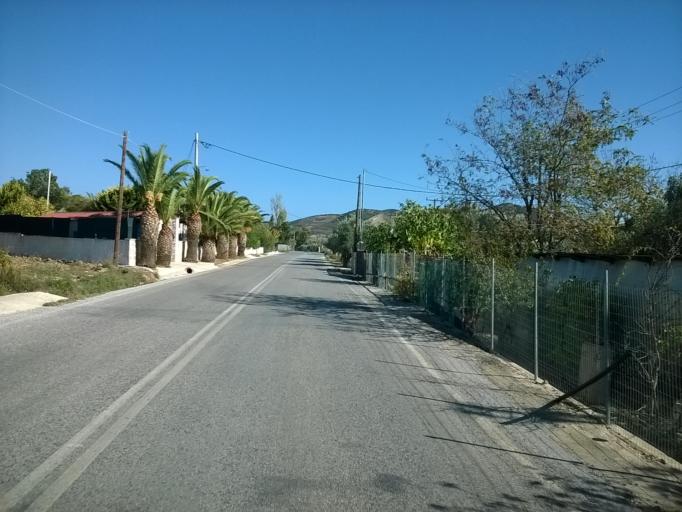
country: GR
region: Attica
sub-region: Nomarchia Anatolikis Attikis
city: Keratea
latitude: 37.7776
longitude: 24.0002
